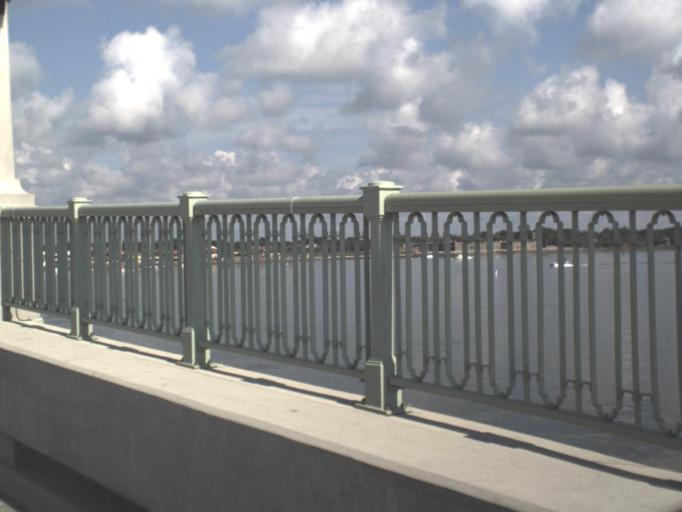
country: US
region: Florida
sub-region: Saint Johns County
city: Saint Augustine
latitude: 29.8930
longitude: -81.3054
